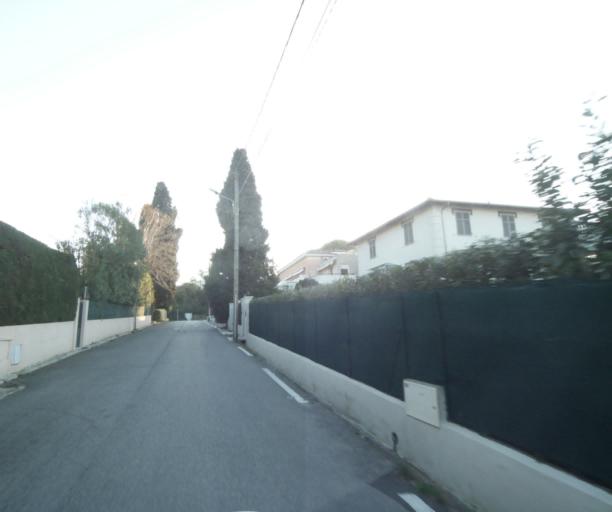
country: FR
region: Provence-Alpes-Cote d'Azur
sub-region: Departement des Alpes-Maritimes
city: Antibes
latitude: 43.5663
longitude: 7.1282
